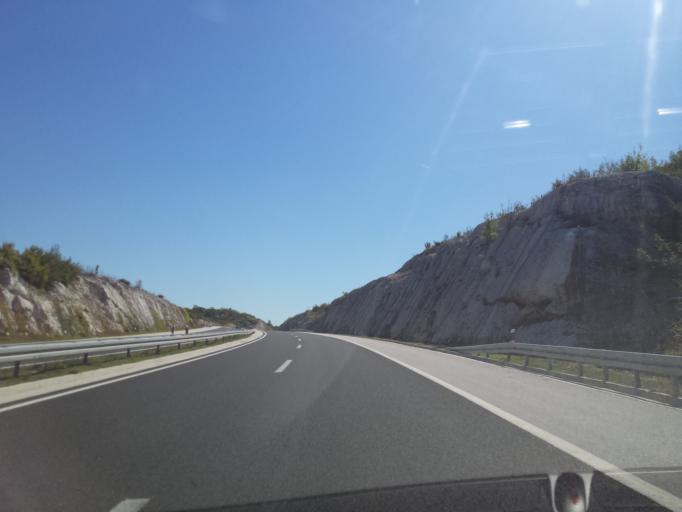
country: HR
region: Splitsko-Dalmatinska
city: Dugopolje
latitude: 43.5876
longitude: 16.6330
